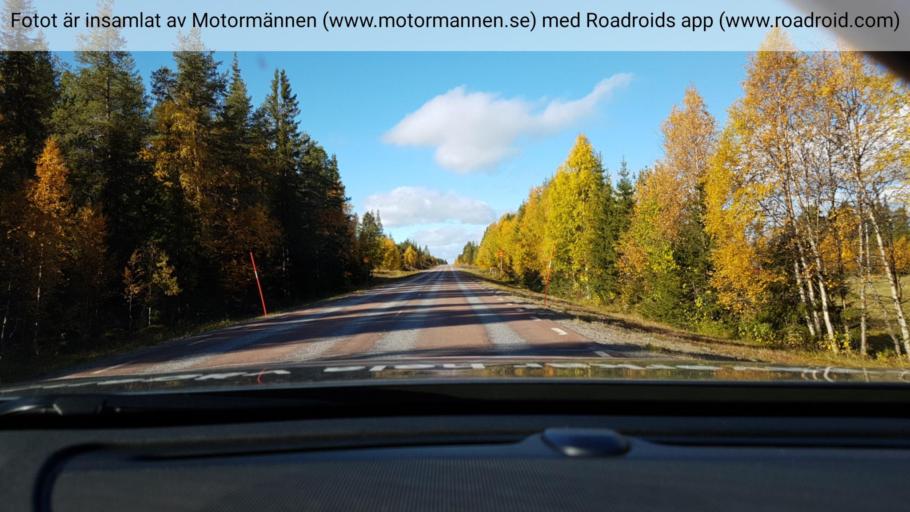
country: SE
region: Norrbotten
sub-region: Arjeplogs Kommun
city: Arjeplog
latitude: 66.0549
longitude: 17.9944
